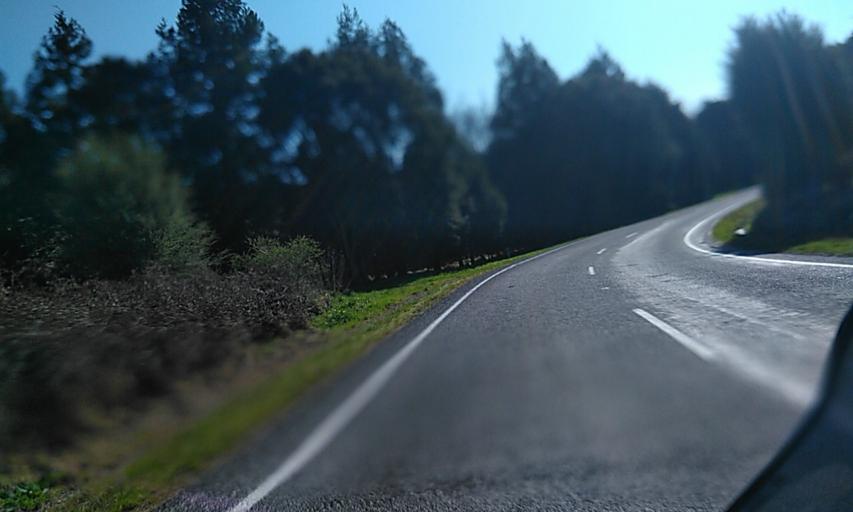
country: NZ
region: Gisborne
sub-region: Gisborne District
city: Gisborne
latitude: -38.5808
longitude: 178.0125
